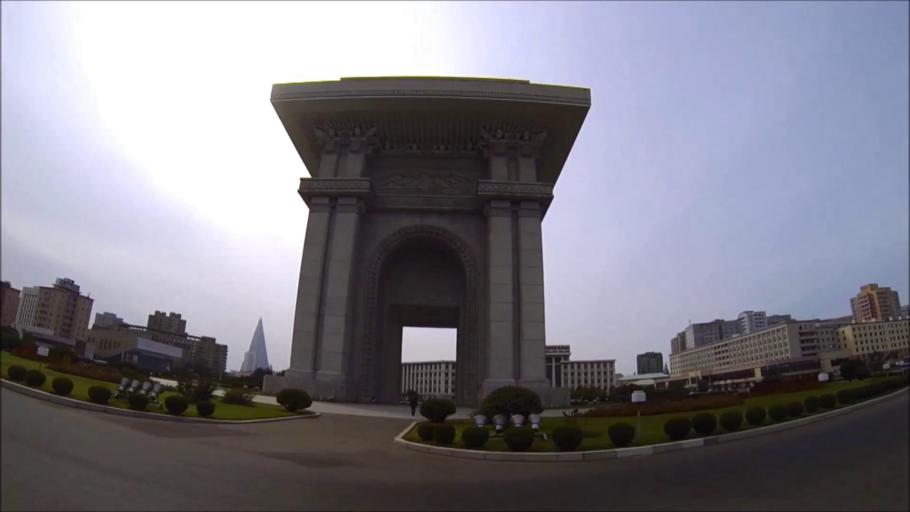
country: KP
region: Pyongyang
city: Pyongyang
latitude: 39.0445
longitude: 125.7542
